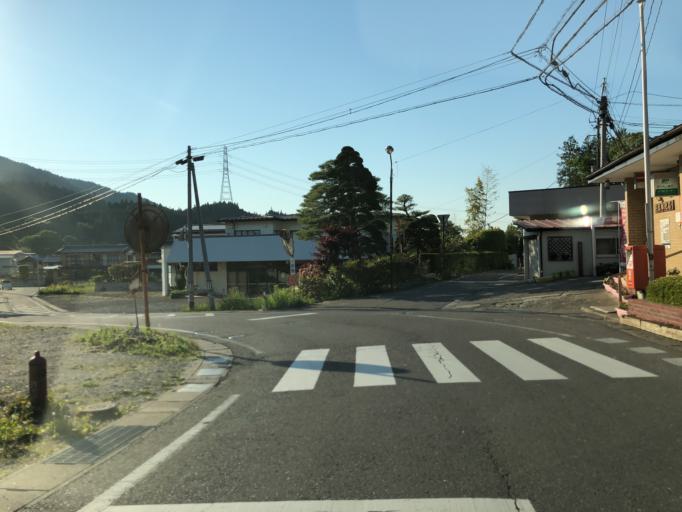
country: JP
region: Ibaraki
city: Daigo
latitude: 36.9402
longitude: 140.4439
